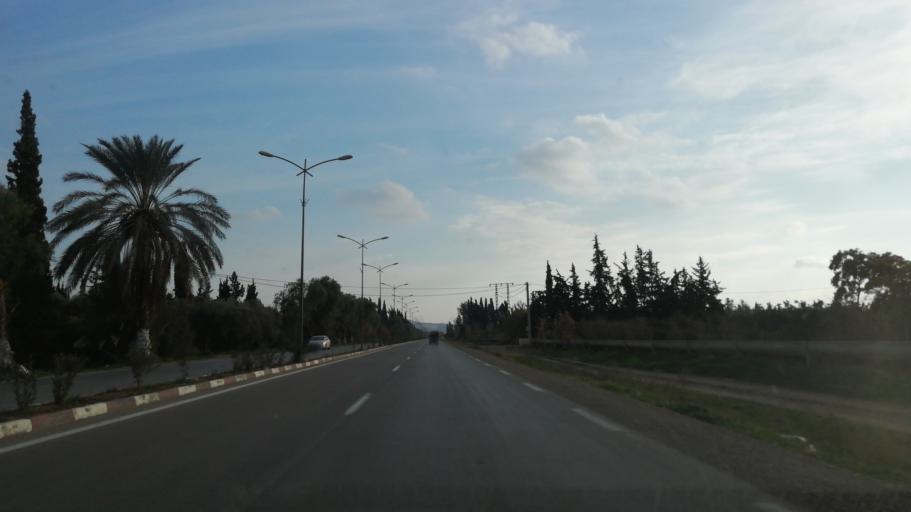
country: DZ
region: Mascara
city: Mascara
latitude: 35.6110
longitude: 0.0629
